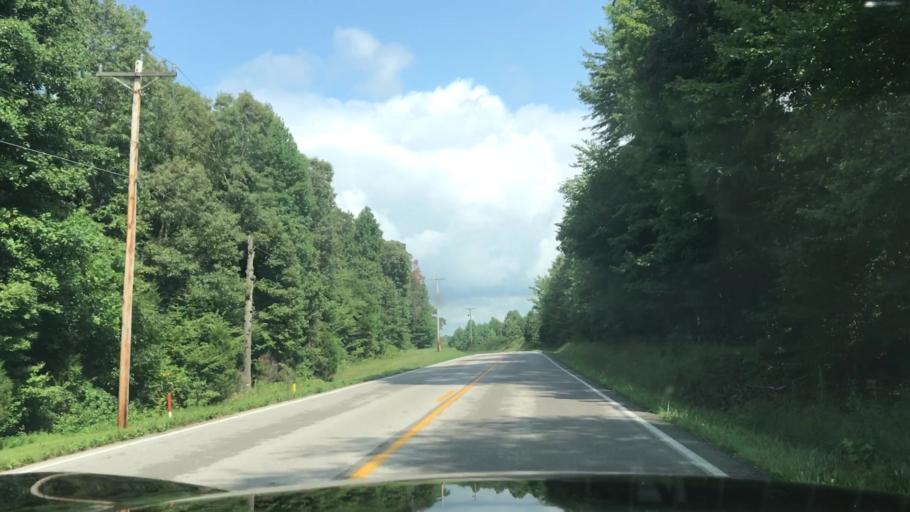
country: US
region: Kentucky
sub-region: Butler County
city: Morgantown
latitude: 37.1880
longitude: -86.8783
